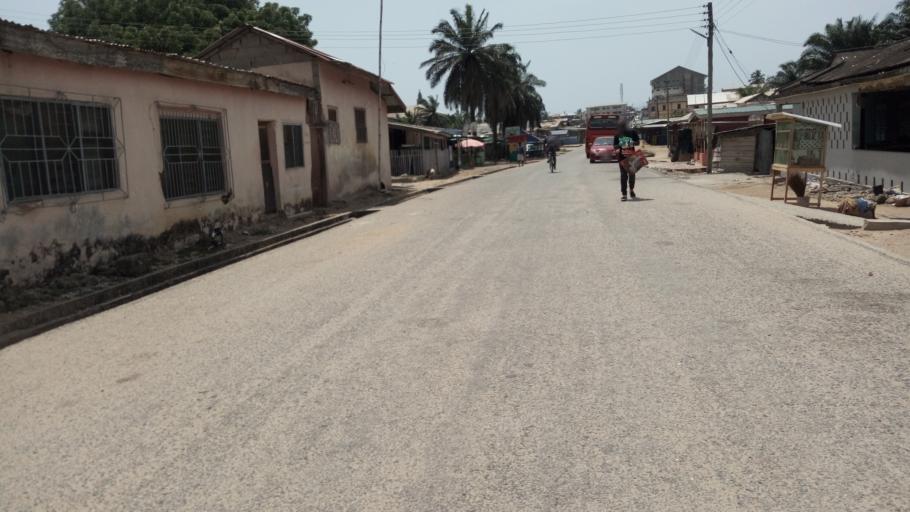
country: GH
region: Central
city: Winneba
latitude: 5.3481
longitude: -0.6278
